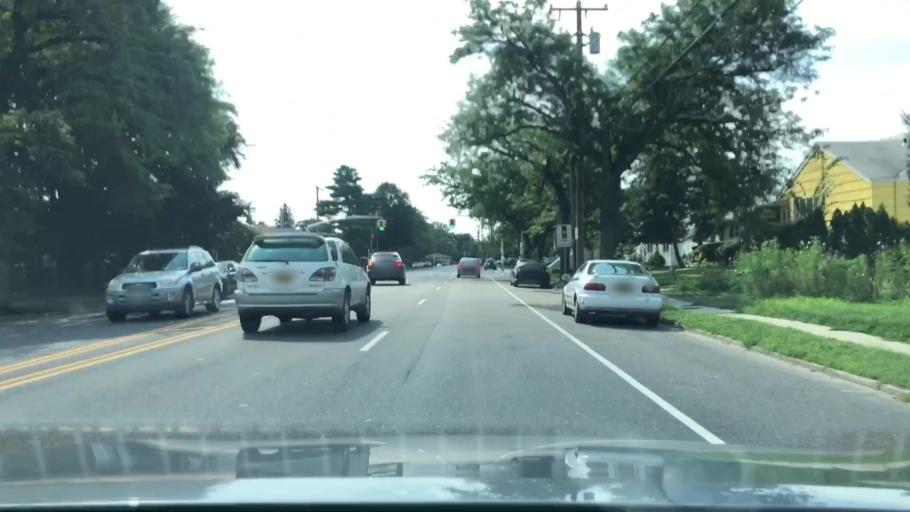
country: US
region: New York
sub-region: Nassau County
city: South Hempstead
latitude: 40.6757
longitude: -73.6130
